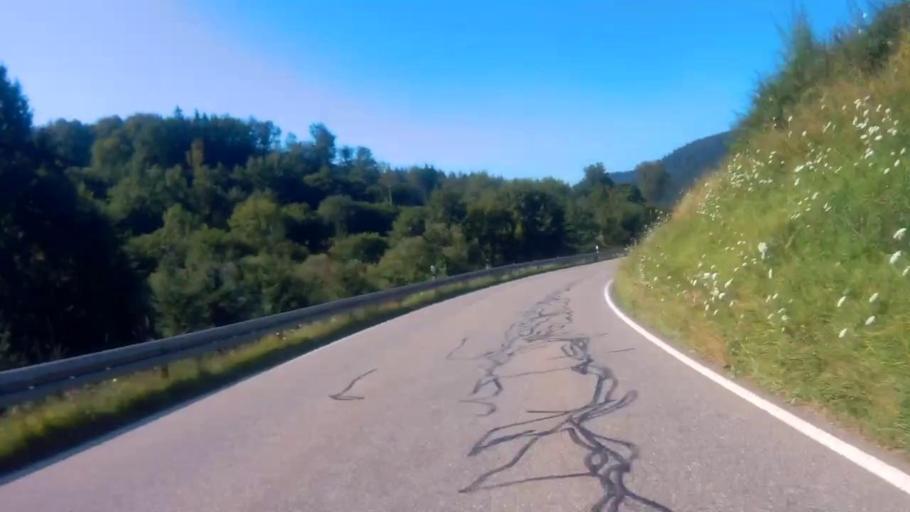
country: DE
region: Baden-Wuerttemberg
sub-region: Freiburg Region
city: Hausen
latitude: 47.6802
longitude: 7.8127
